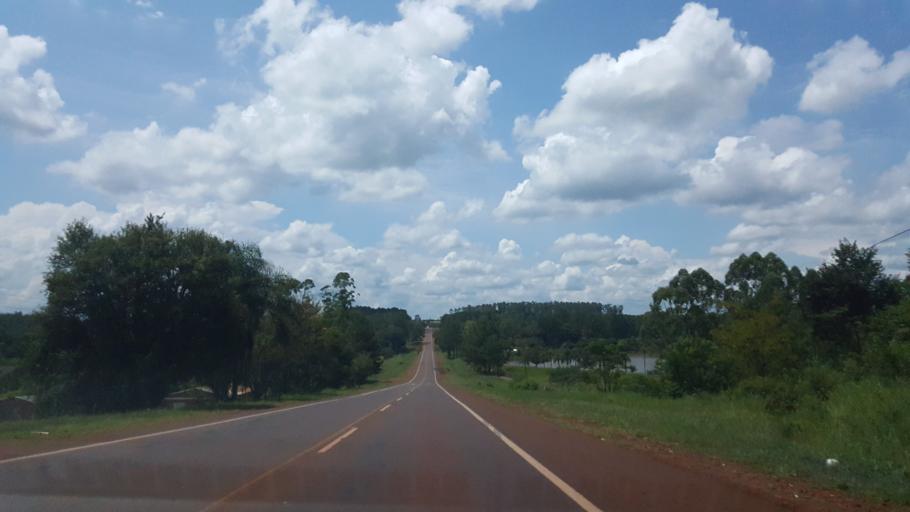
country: AR
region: Misiones
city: Garuhape
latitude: -26.8181
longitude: -54.9509
